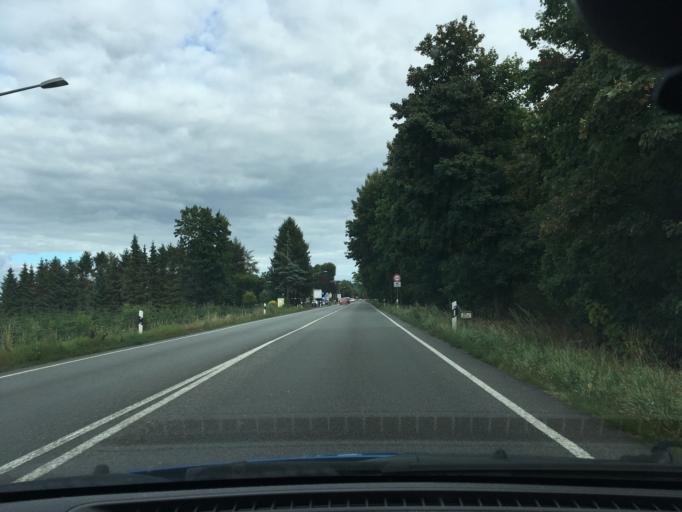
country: DE
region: Lower Saxony
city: Buxtehude
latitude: 53.4523
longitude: 9.7424
